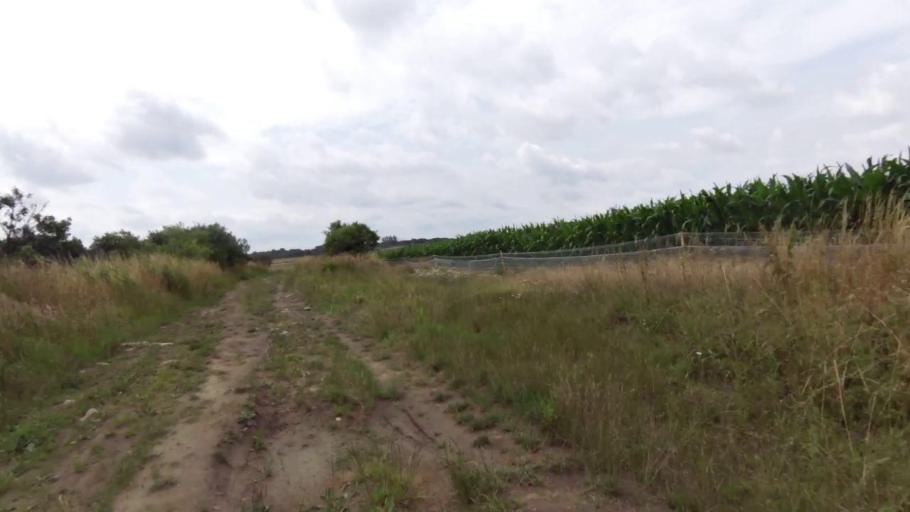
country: PL
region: West Pomeranian Voivodeship
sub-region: Powiat mysliborski
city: Mysliborz
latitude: 52.9818
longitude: 14.9015
